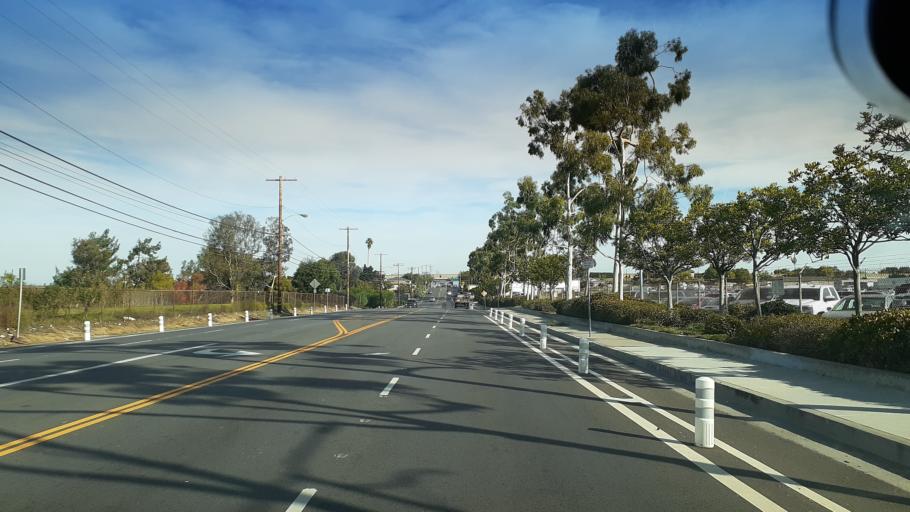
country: US
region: California
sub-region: Los Angeles County
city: Lomita
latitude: 33.7787
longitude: -118.2858
